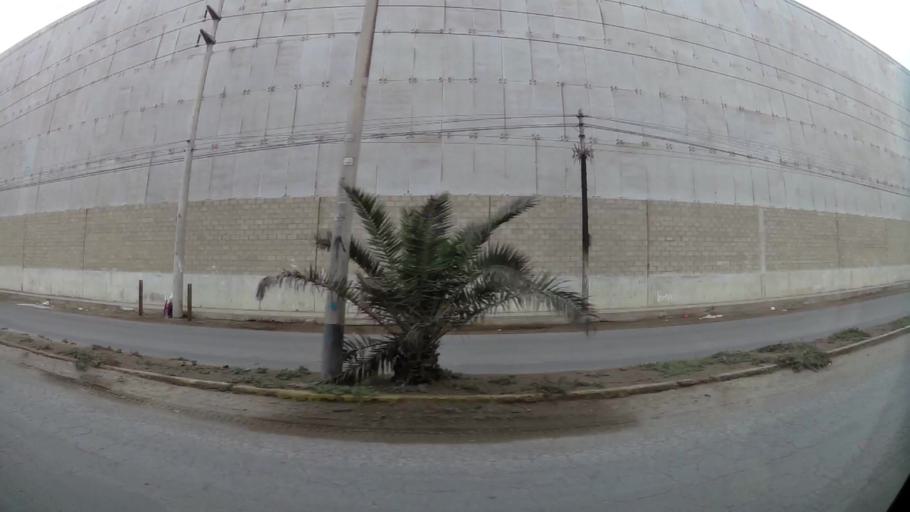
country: PE
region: Lima
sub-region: Lima
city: Punta Hermosa
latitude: -12.2960
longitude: -76.8389
